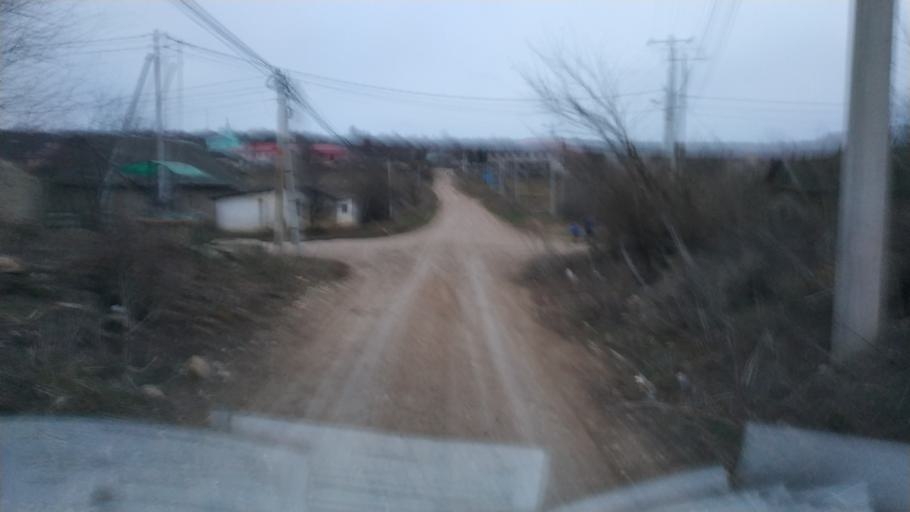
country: MD
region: Causeni
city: Causeni
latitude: 46.4995
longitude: 29.4063
